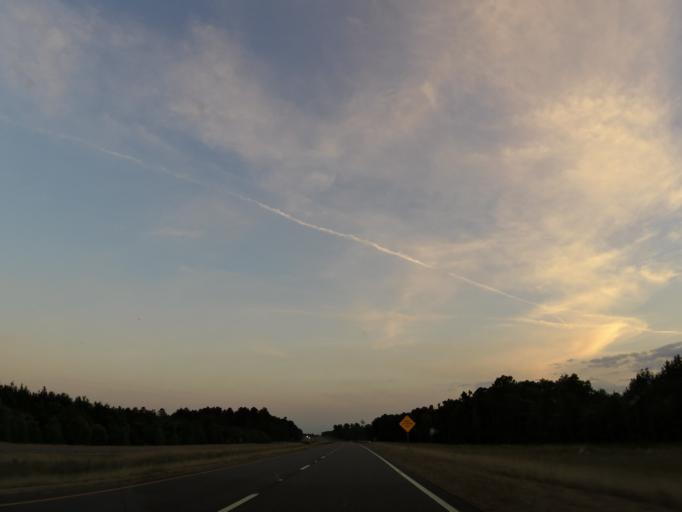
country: US
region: Mississippi
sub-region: Kemper County
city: De Kalb
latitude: 32.7613
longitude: -88.4654
